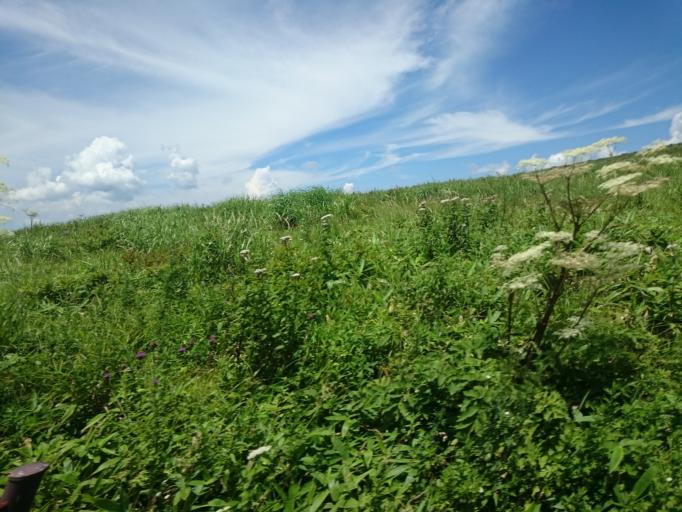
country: JP
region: Nagano
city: Suwa
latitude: 36.1009
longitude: 138.1825
